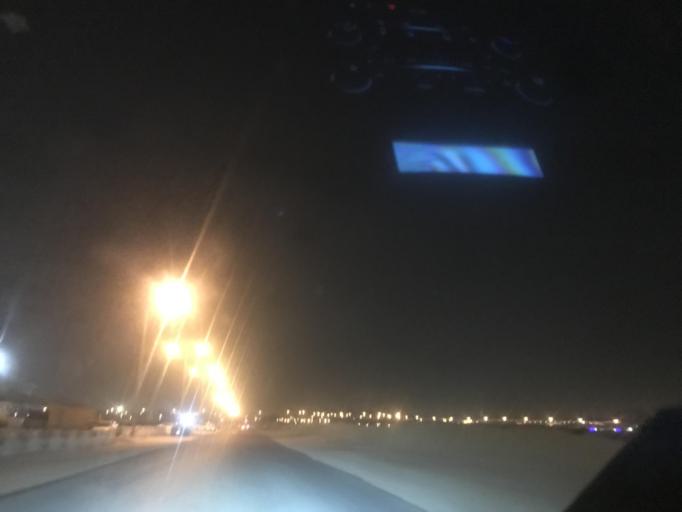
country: SA
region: Ar Riyad
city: Riyadh
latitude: 24.7628
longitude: 46.5884
